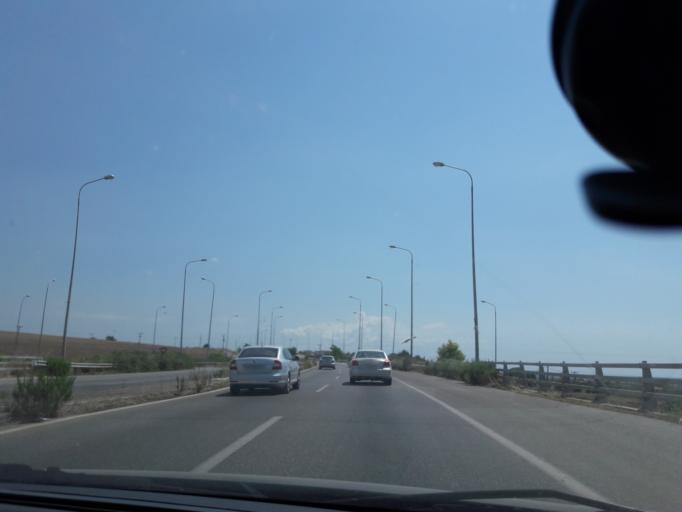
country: GR
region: Central Macedonia
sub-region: Nomos Chalkidikis
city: Nea Plagia
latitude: 40.2871
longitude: 23.1481
